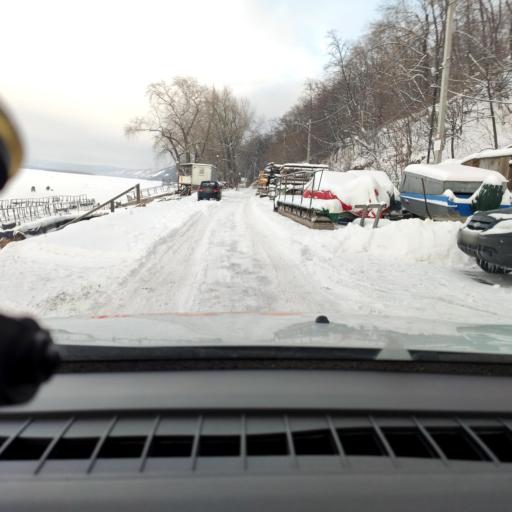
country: RU
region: Samara
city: Samara
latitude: 53.2872
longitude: 50.1909
